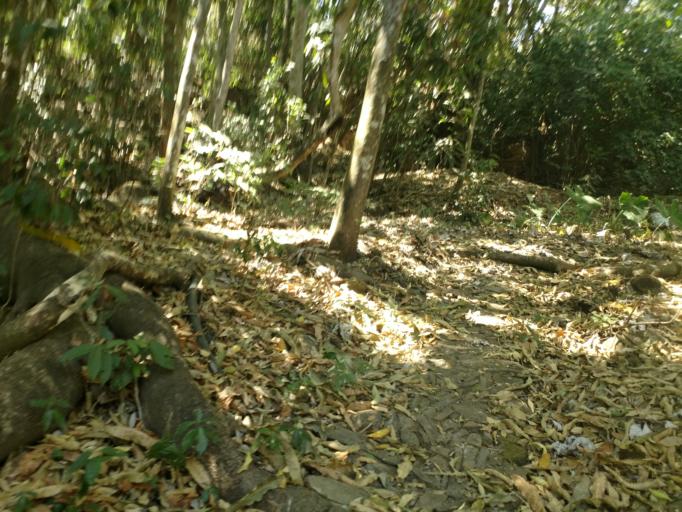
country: MX
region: Nayarit
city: Tepic
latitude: 21.5663
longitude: -104.9997
